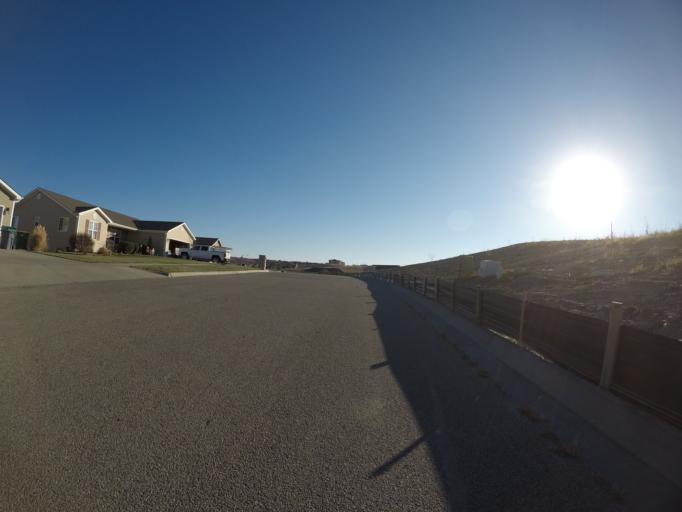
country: US
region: Kansas
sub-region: Riley County
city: Manhattan
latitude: 39.1832
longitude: -96.6479
